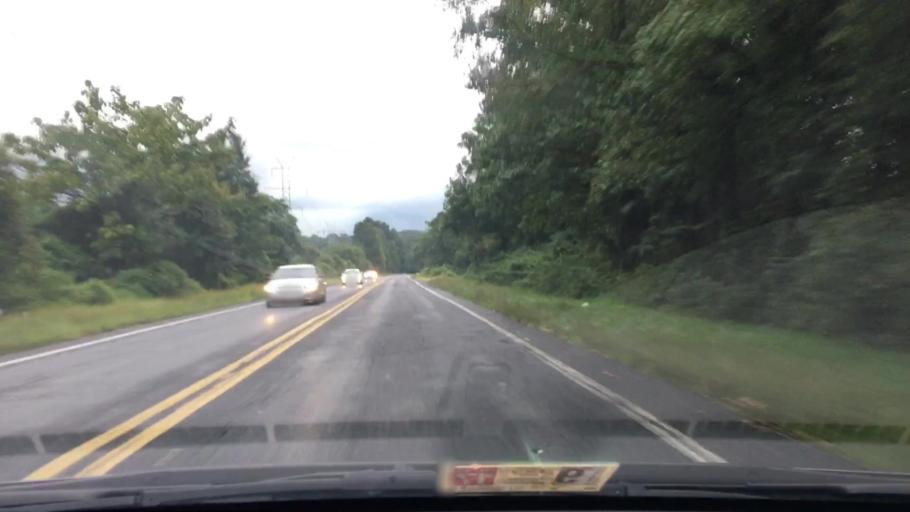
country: US
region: Maryland
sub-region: Montgomery County
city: Redland
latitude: 39.1850
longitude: -77.1461
